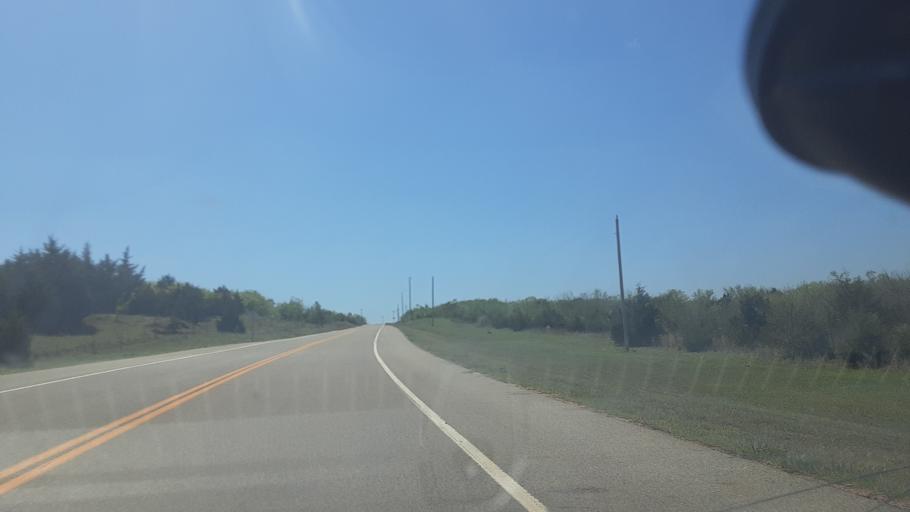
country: US
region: Oklahoma
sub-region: Logan County
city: Guthrie
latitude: 36.0482
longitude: -97.4069
